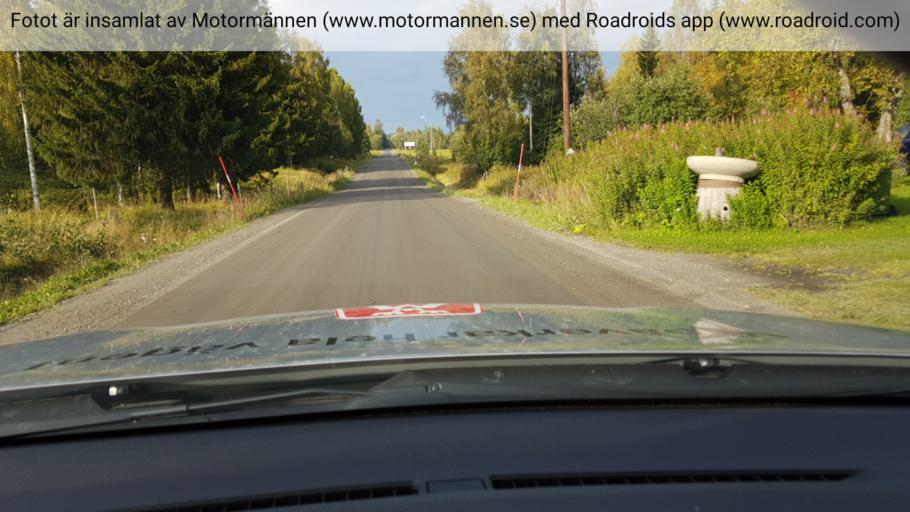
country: SE
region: Jaemtland
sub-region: Stroemsunds Kommun
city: Stroemsund
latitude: 64.0341
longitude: 15.8096
